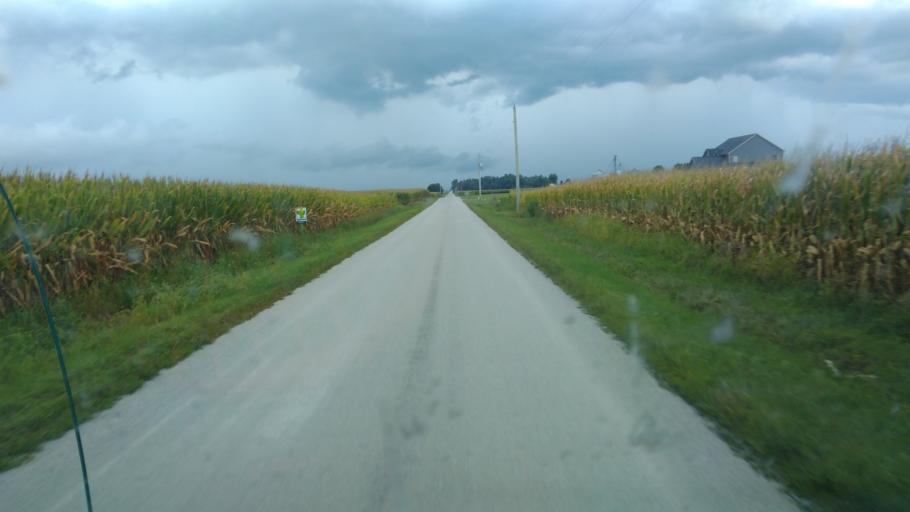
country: US
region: Ohio
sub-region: Hardin County
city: Kenton
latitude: 40.6533
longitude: -83.5150
